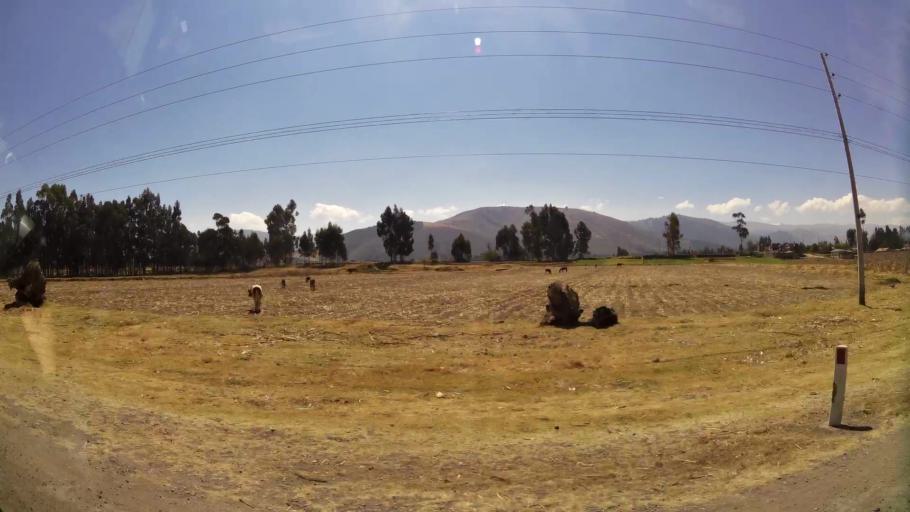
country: PE
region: Junin
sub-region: Provincia de Concepcion
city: Matahuasi
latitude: -11.8821
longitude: -75.3549
